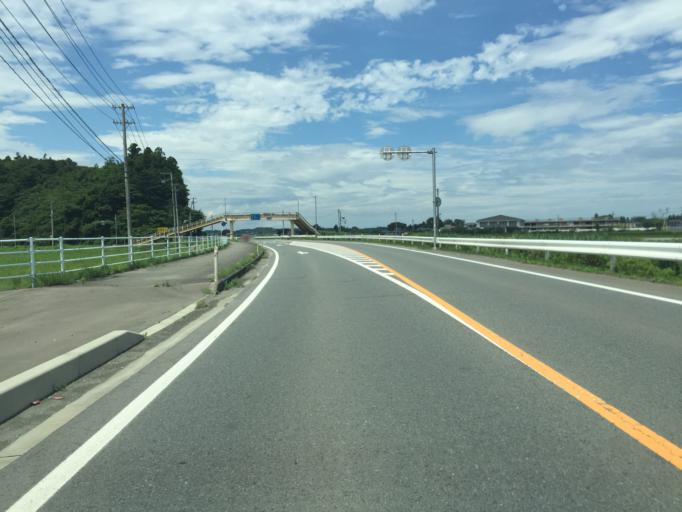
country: JP
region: Fukushima
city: Namie
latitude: 37.6852
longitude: 140.9807
